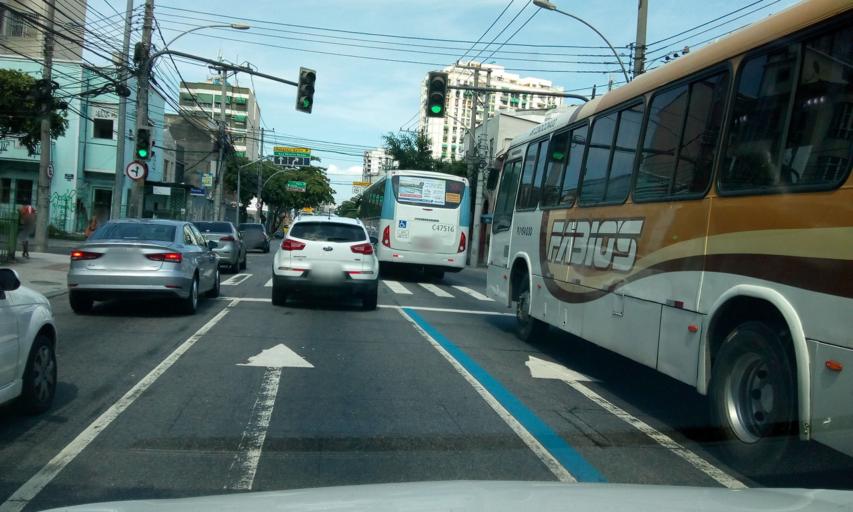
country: BR
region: Rio de Janeiro
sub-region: Rio De Janeiro
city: Rio de Janeiro
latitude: -22.9169
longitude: -43.2421
